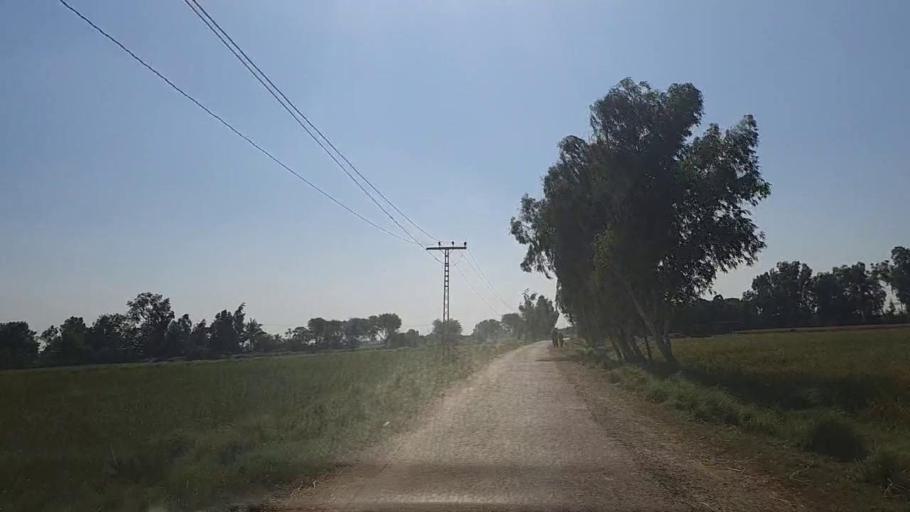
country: PK
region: Sindh
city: Thatta
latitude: 24.7771
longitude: 67.9470
